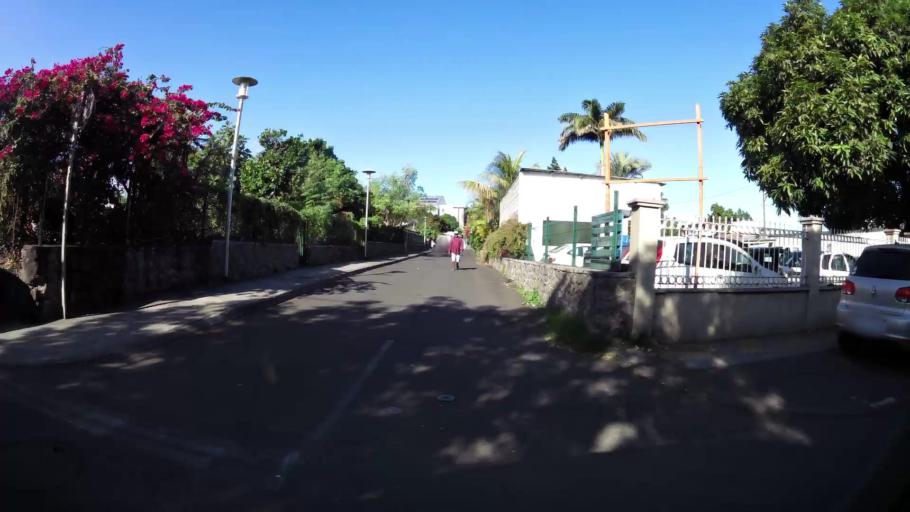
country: RE
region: Reunion
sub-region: Reunion
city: Saint-Louis
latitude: -21.2901
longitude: 55.4102
